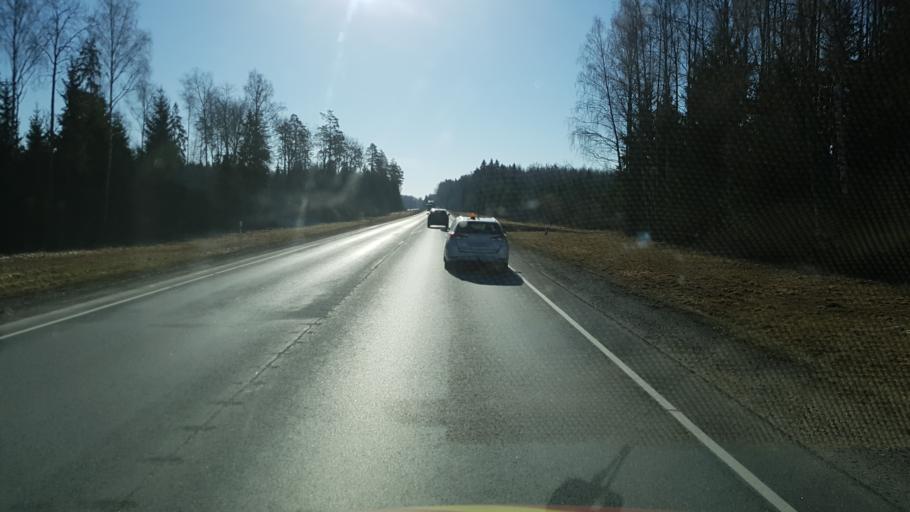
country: EE
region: Jogevamaa
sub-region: Poltsamaa linn
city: Poltsamaa
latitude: 58.6215
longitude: 26.1641
